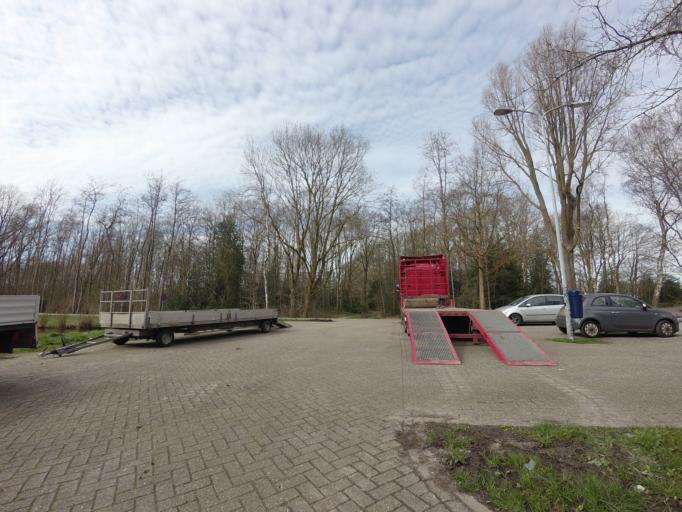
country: NL
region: North Holland
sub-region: Gemeente Uithoorn
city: Uithoorn
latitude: 52.2460
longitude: 4.8412
